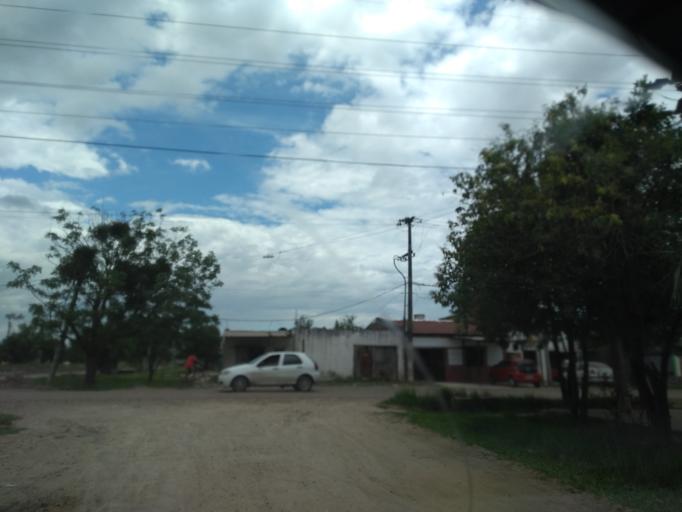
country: AR
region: Chaco
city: Resistencia
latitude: -27.4742
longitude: -58.9697
